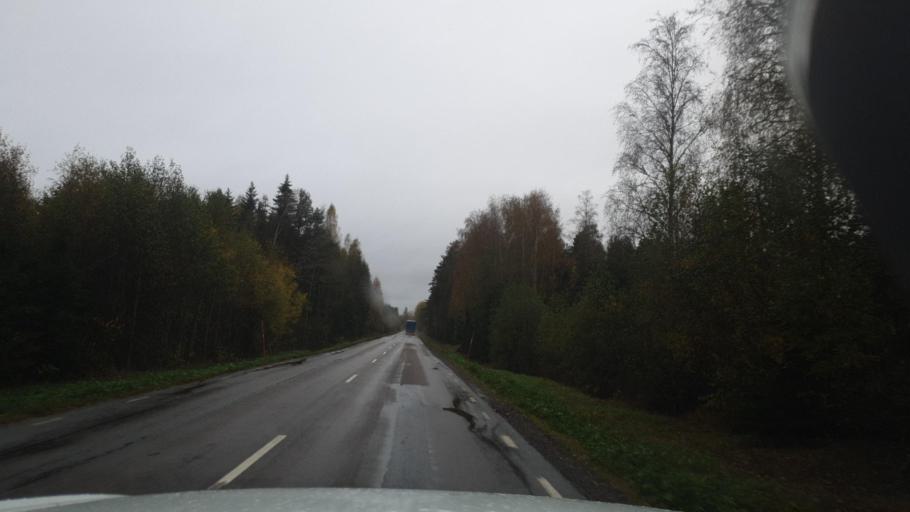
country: SE
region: Vaermland
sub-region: Eda Kommun
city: Charlottenberg
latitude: 59.8260
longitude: 12.2628
